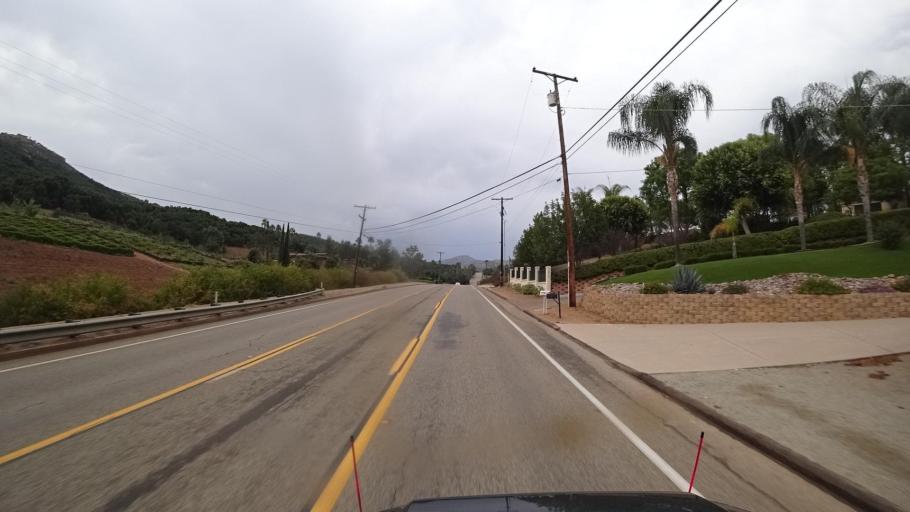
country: US
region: California
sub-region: San Diego County
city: San Pasqual
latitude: 33.1109
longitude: -117.0185
